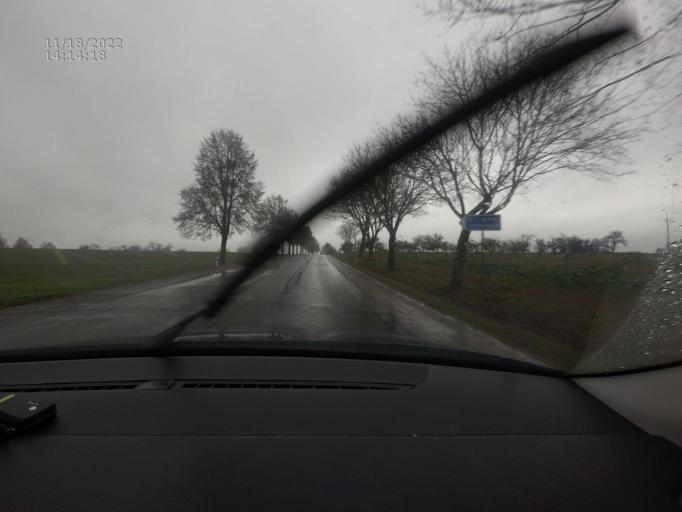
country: CZ
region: Jihocesky
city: Mirotice
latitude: 49.4179
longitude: 14.0354
